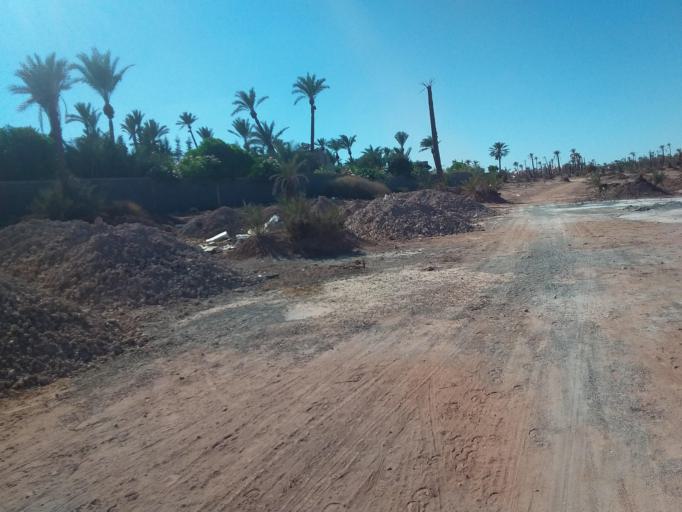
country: MA
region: Marrakech-Tensift-Al Haouz
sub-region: Marrakech
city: Marrakesh
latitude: 31.6801
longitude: -7.9546
